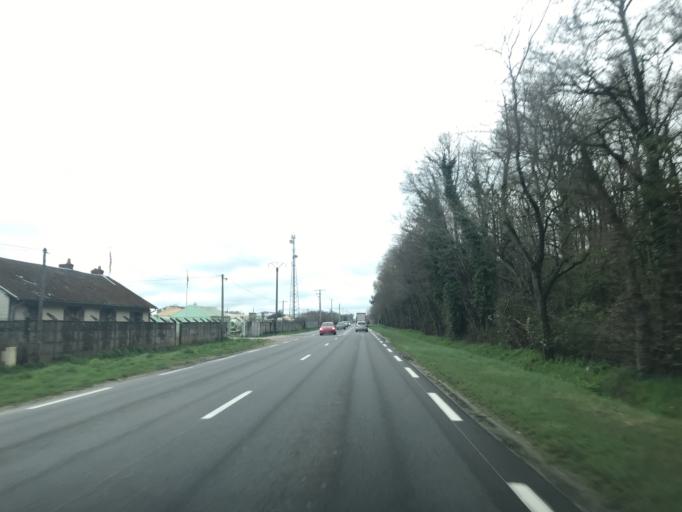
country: FR
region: Centre
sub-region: Departement du Loiret
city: Bray-en-Val
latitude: 47.8419
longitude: 2.3300
